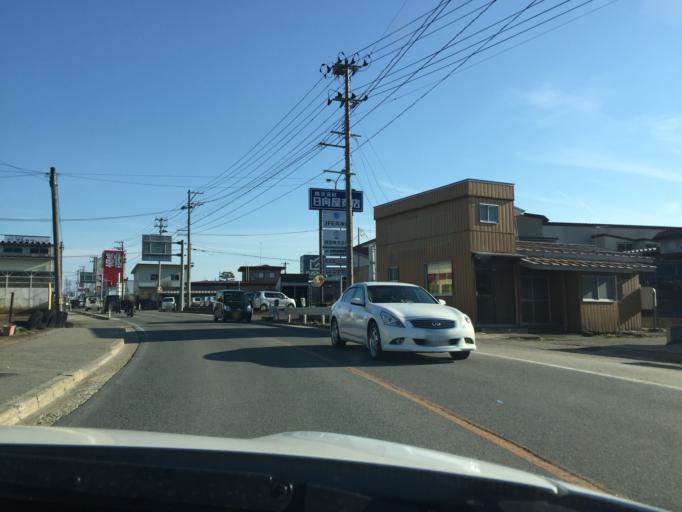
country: JP
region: Yamagata
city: Nagai
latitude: 38.0944
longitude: 140.0415
